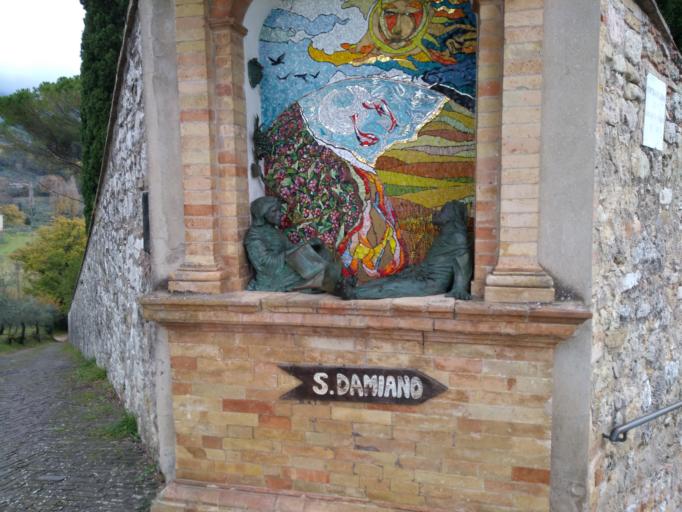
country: IT
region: Umbria
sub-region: Provincia di Perugia
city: Assisi
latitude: 43.0625
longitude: 12.6182
